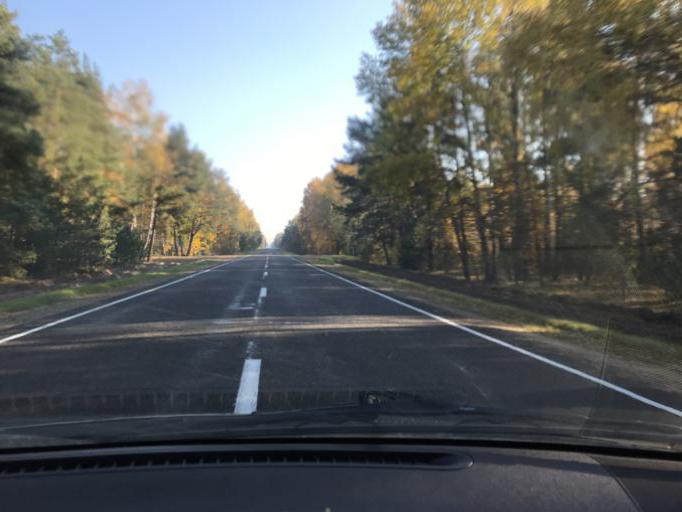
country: BY
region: Brest
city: Baranovichi
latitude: 52.9136
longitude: 25.9422
